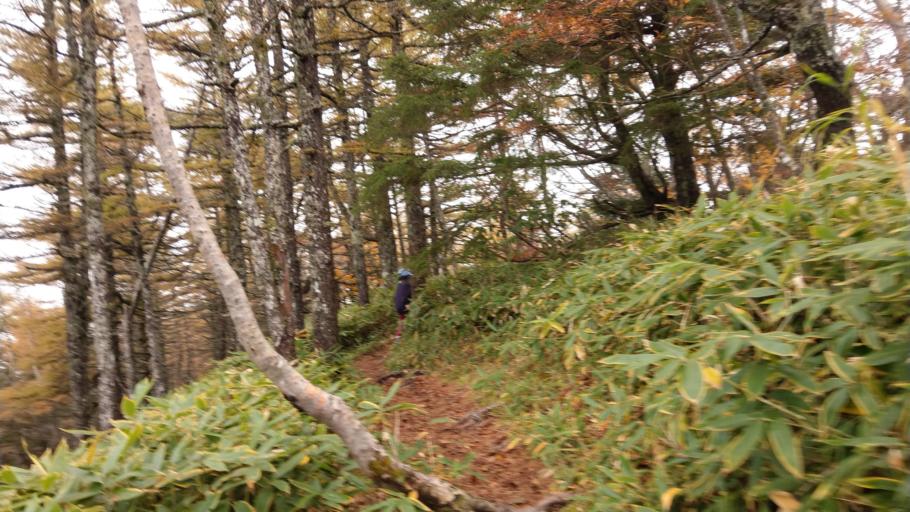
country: JP
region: Nagano
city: Komoro
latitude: 36.4013
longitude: 138.4571
